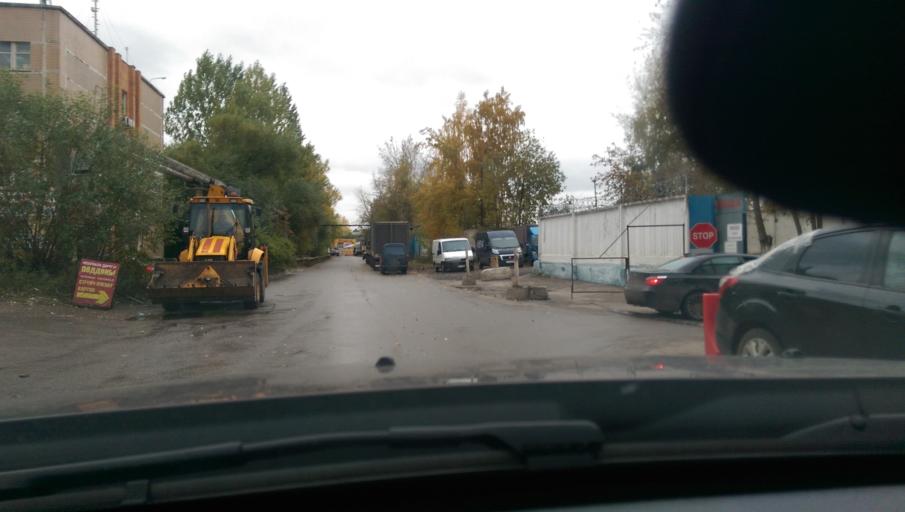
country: RU
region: Moscow
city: Altuf'yevskiy
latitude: 55.8892
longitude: 37.5736
